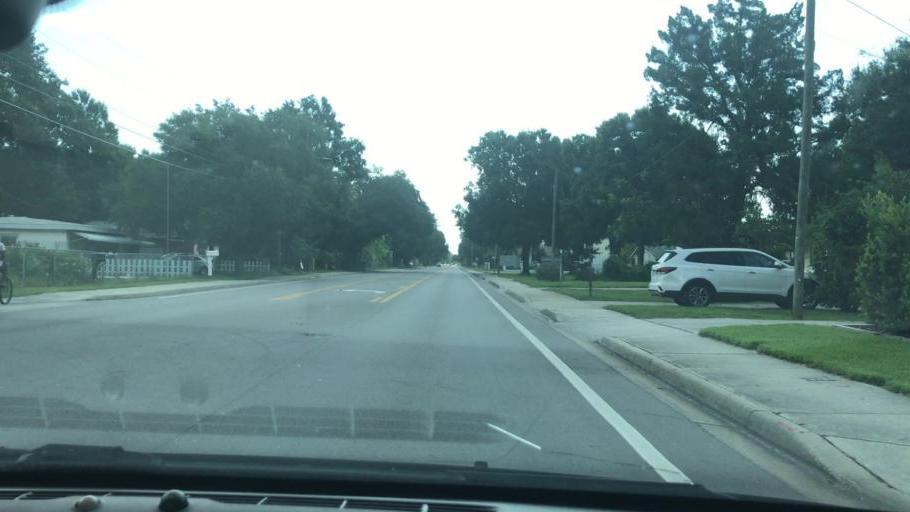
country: US
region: Florida
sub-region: Pinellas County
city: Pinellas Park
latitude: 27.8429
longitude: -82.6940
